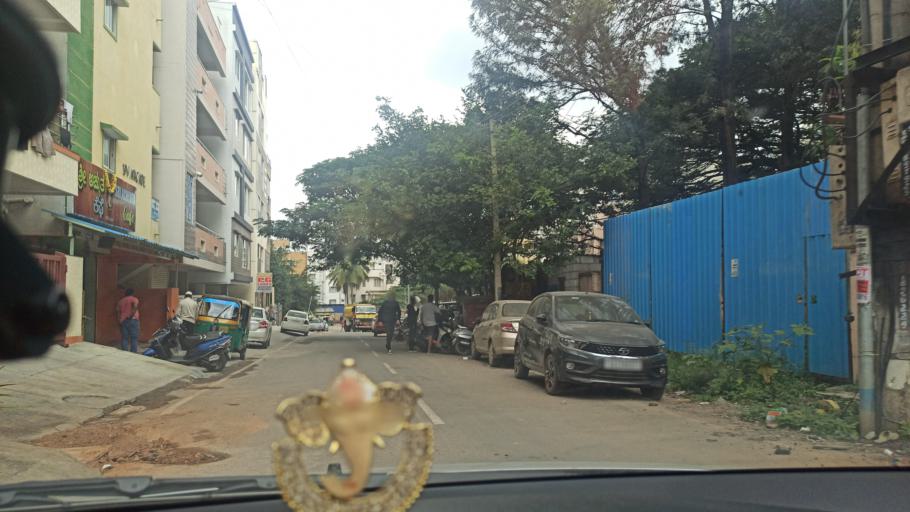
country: IN
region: Karnataka
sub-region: Bangalore Urban
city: Bangalore
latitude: 12.9213
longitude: 77.6473
